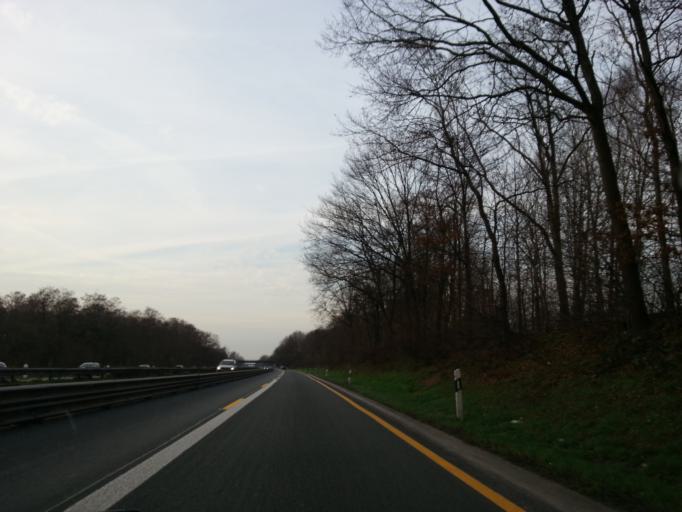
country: DE
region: North Rhine-Westphalia
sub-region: Regierungsbezirk Munster
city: Isselburg
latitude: 51.8210
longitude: 6.4252
